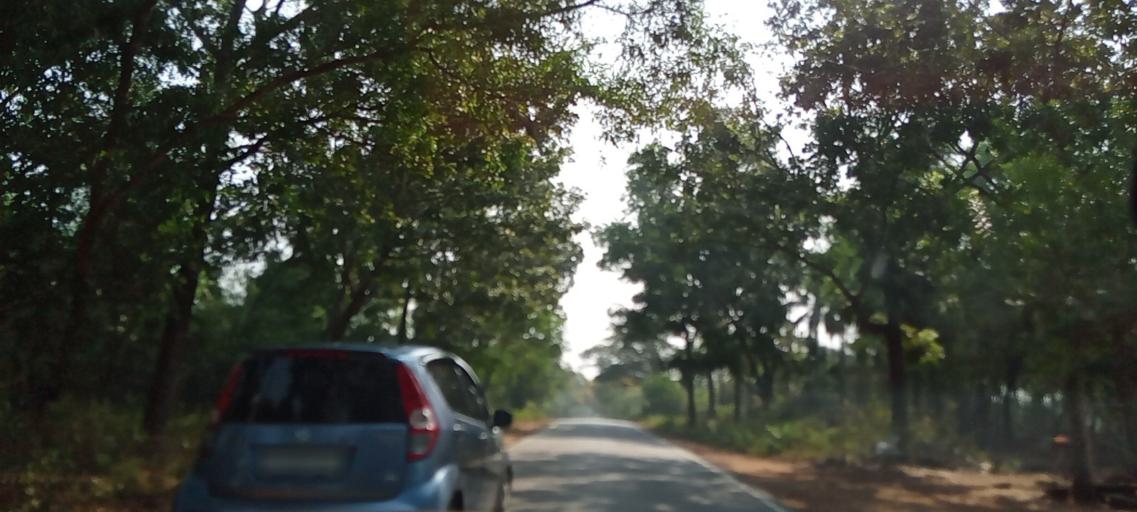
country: IN
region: Karnataka
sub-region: Udupi
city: Coondapoor
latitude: 13.5117
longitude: 74.7780
